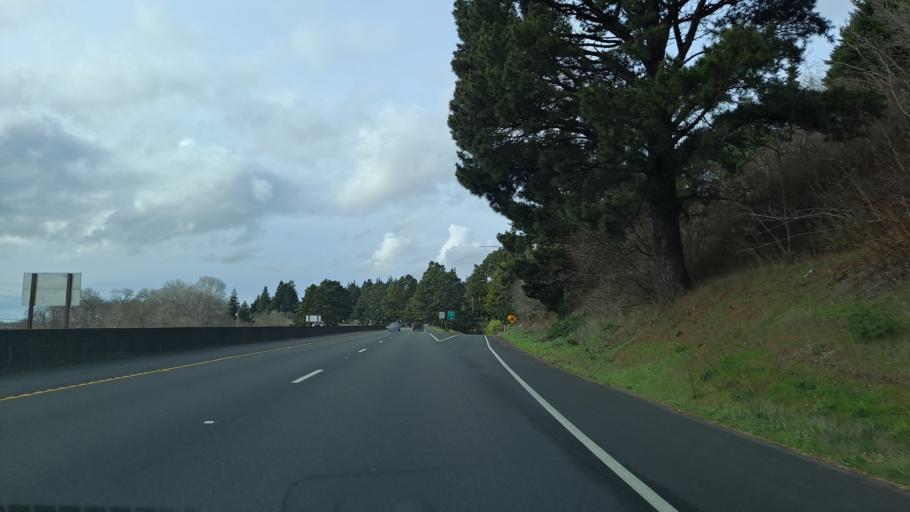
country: US
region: California
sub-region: Humboldt County
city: Fortuna
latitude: 40.6035
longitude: -124.1753
